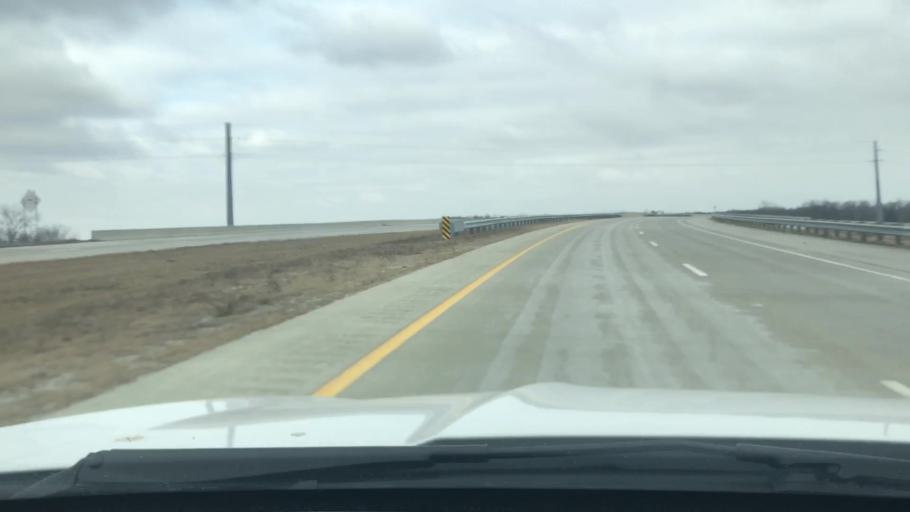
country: US
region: Indiana
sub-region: Carroll County
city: Delphi
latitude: 40.5972
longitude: -86.6552
